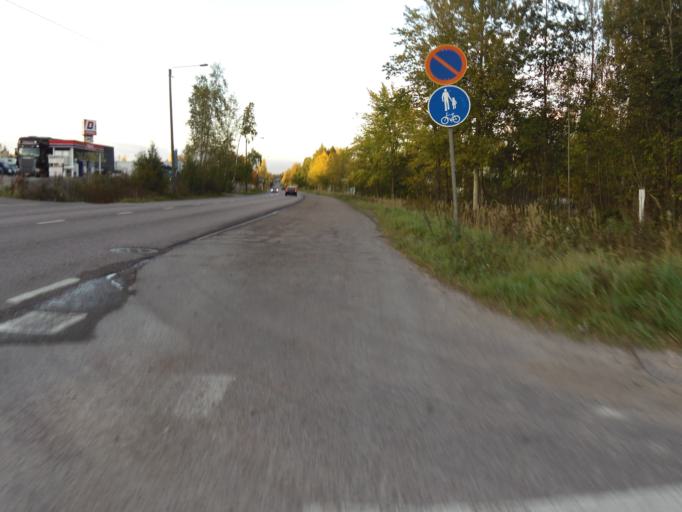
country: FI
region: Uusimaa
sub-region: Helsinki
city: Kilo
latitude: 60.2721
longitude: 24.7604
